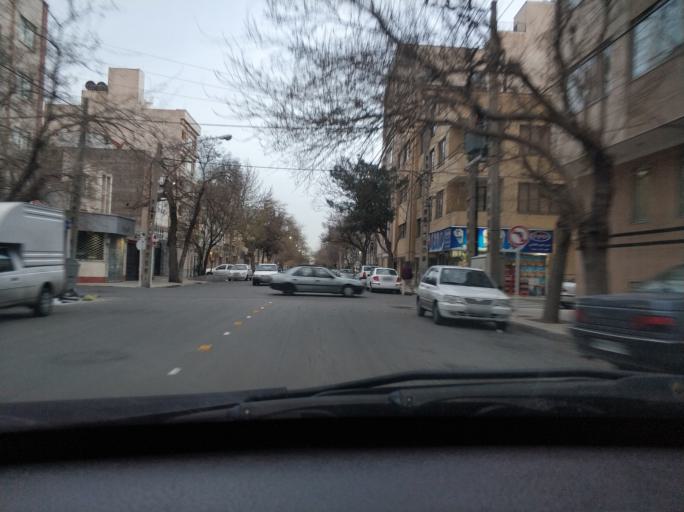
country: IR
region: Razavi Khorasan
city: Mashhad
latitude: 36.2731
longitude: 59.5976
